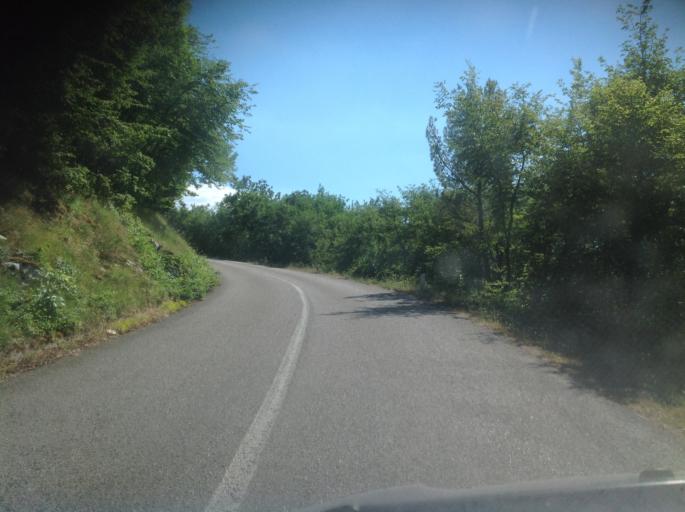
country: IT
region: Umbria
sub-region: Provincia di Terni
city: Stroncone
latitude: 42.4856
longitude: 12.6627
